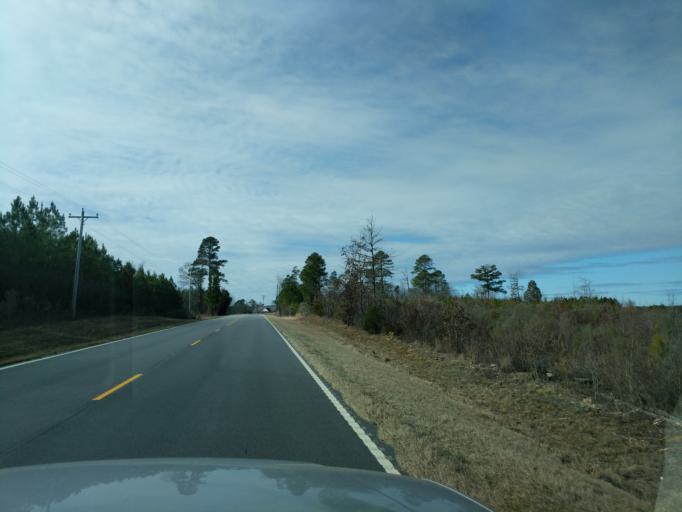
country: US
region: South Carolina
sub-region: Edgefield County
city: Edgefield
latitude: 33.9351
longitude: -81.9655
